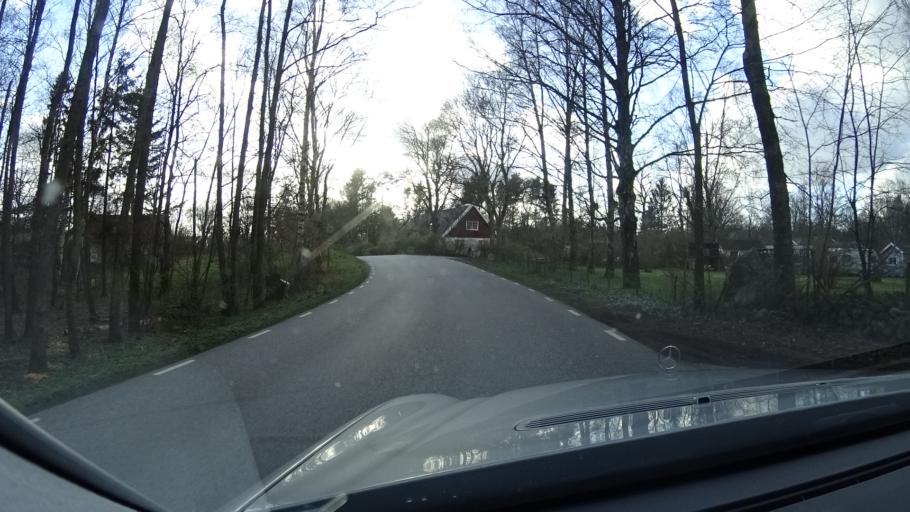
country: SE
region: Skane
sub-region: Hoors Kommun
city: Satofta
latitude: 55.9033
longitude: 13.5933
